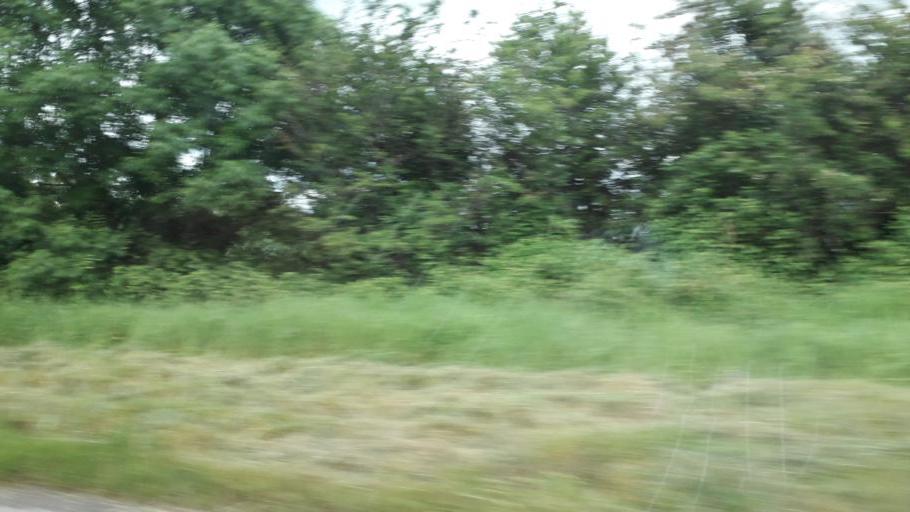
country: IE
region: Leinster
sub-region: County Carlow
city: Bagenalstown
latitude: 52.7407
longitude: -6.9835
